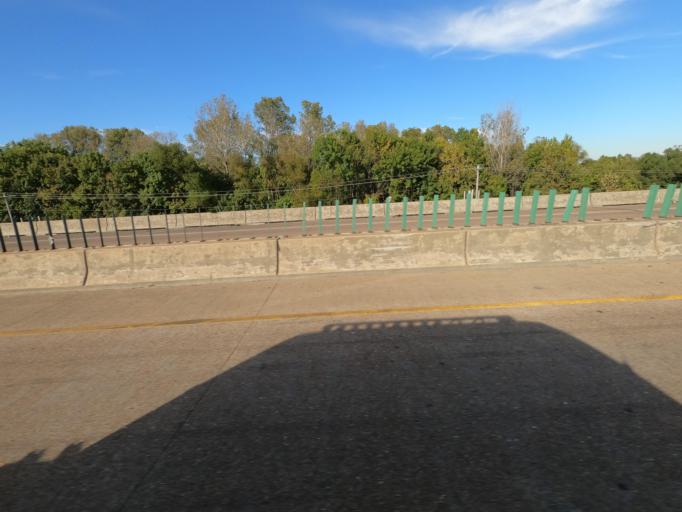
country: US
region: Tennessee
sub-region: Shelby County
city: Memphis
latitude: 35.1432
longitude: -90.1144
